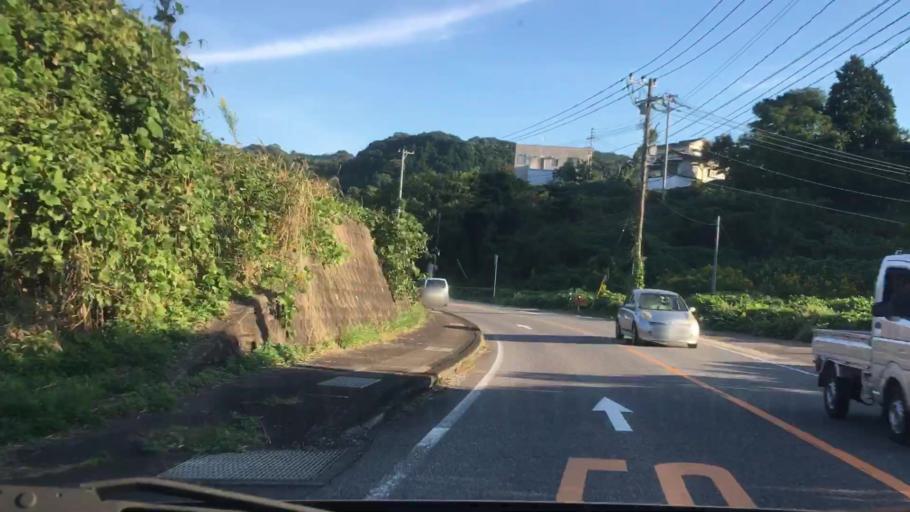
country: JP
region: Nagasaki
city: Sasebo
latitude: 33.0462
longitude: 129.7262
